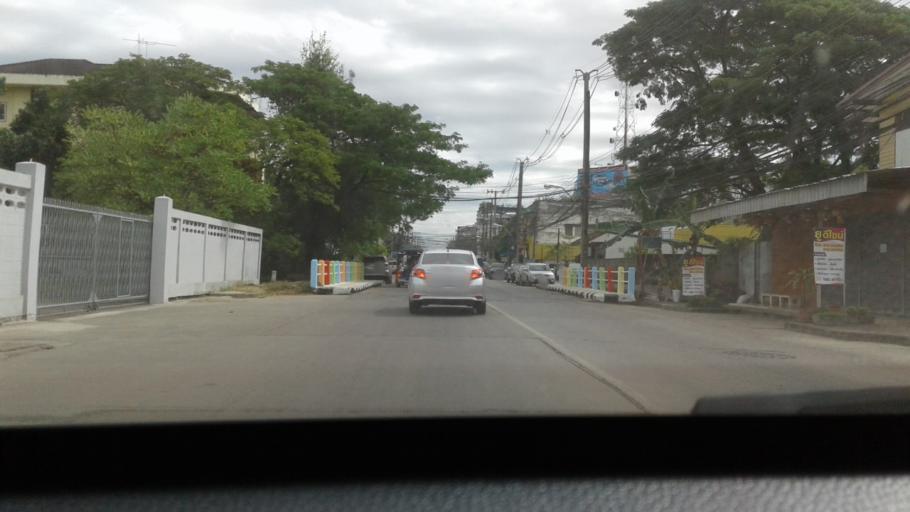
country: TH
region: Changwat Udon Thani
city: Udon Thani
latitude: 17.4143
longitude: 102.7905
